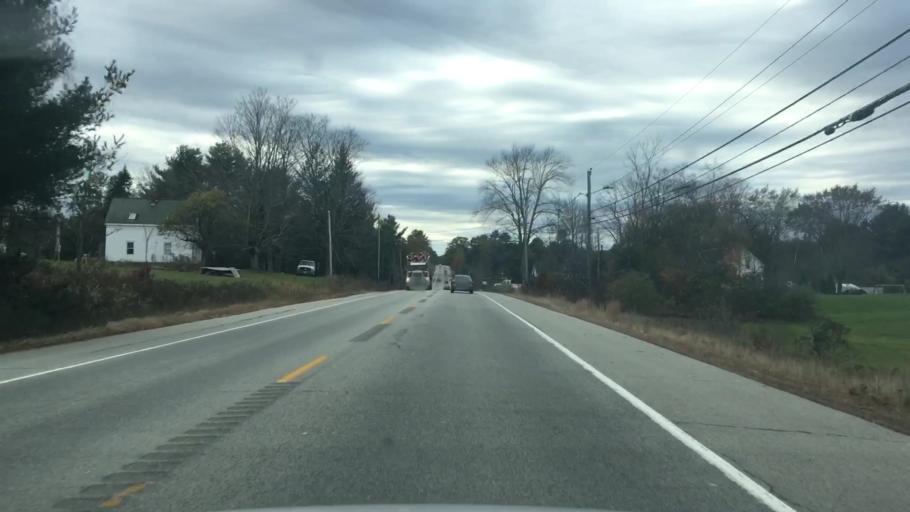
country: US
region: Maine
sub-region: York County
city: West Kennebunk
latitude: 43.4782
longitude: -70.5693
